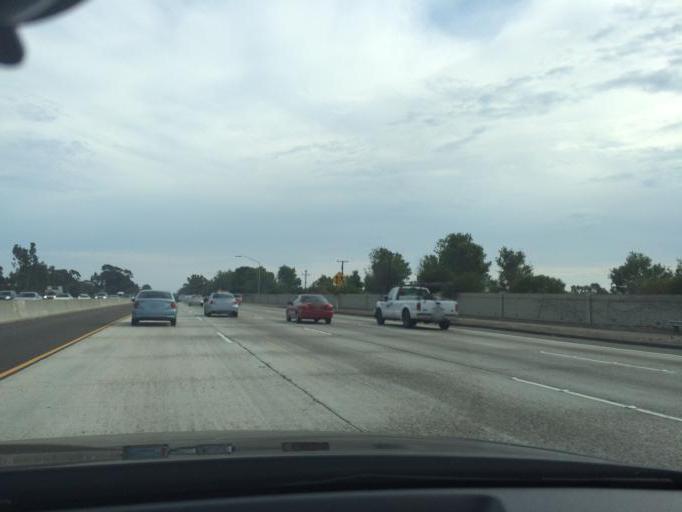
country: US
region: California
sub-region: San Diego County
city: San Diego
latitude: 32.7988
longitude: -117.1566
